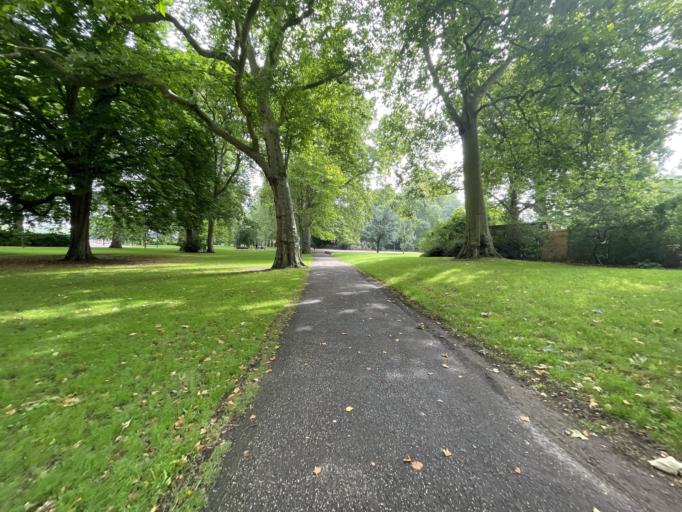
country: GB
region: England
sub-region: Greater London
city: Chelsea
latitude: 51.4812
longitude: -0.1634
